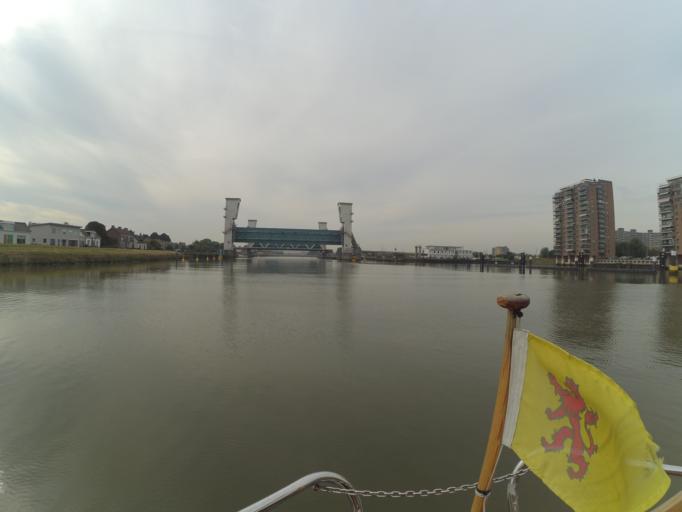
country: NL
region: South Holland
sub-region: Gemeente Capelle aan den IJssel
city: Capelle aan den IJssel
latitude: 51.9197
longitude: 4.5809
